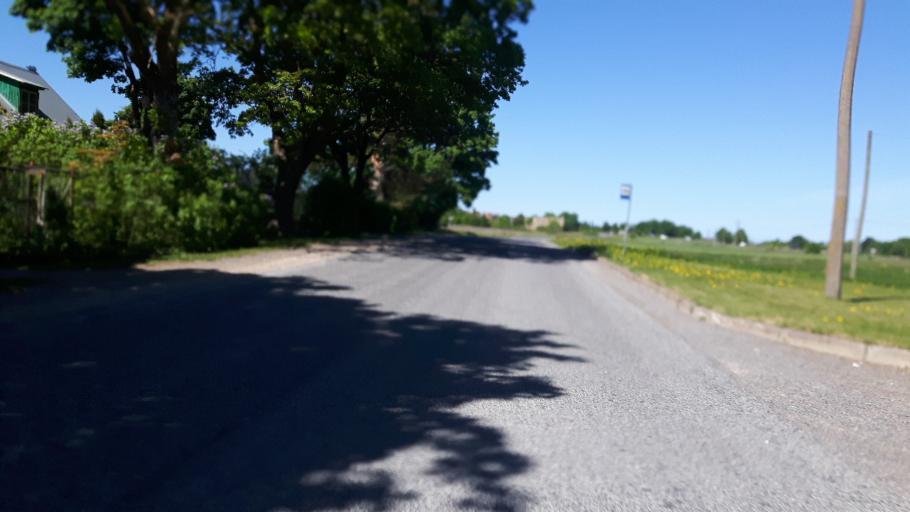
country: EE
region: Ida-Virumaa
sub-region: Sillamaee linn
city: Sillamae
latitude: 59.3835
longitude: 27.8138
